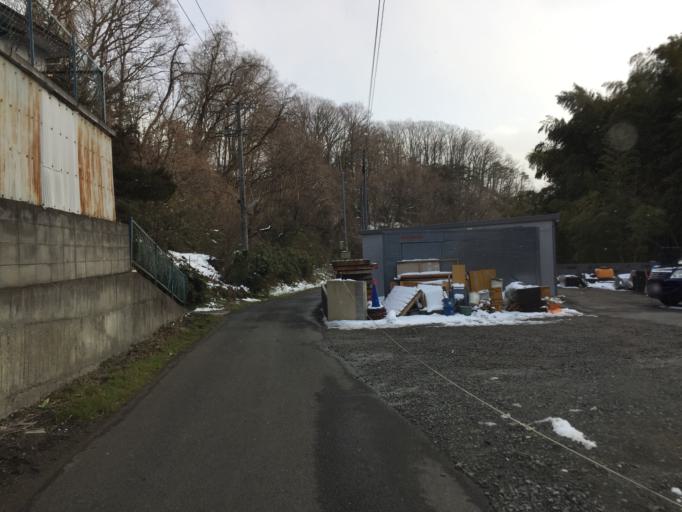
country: JP
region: Fukushima
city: Fukushima-shi
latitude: 37.8359
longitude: 140.4583
